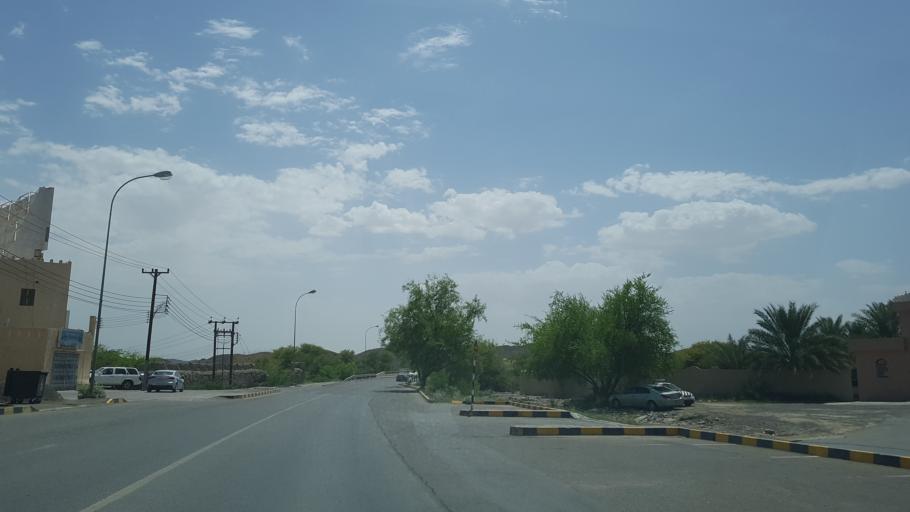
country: OM
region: Muhafazat ad Dakhiliyah
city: Bahla'
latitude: 22.9620
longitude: 57.2984
